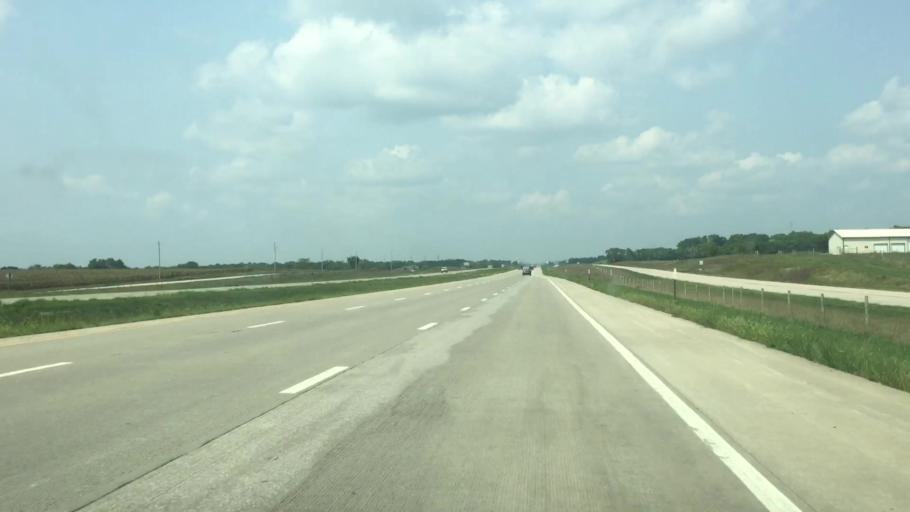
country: US
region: Kansas
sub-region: Douglas County
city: Baldwin City
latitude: 38.7856
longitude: -95.2687
